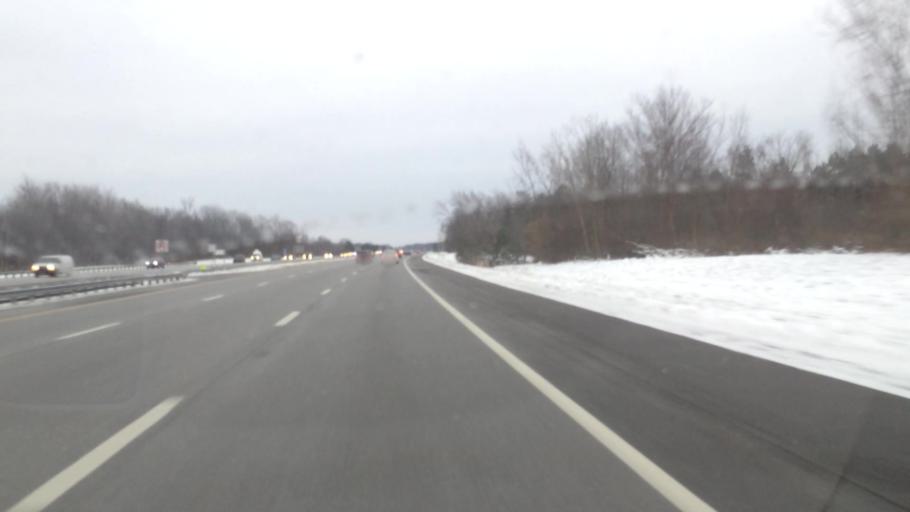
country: US
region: Ohio
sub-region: Cuyahoga County
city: Strongsville
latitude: 41.3028
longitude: -81.8087
